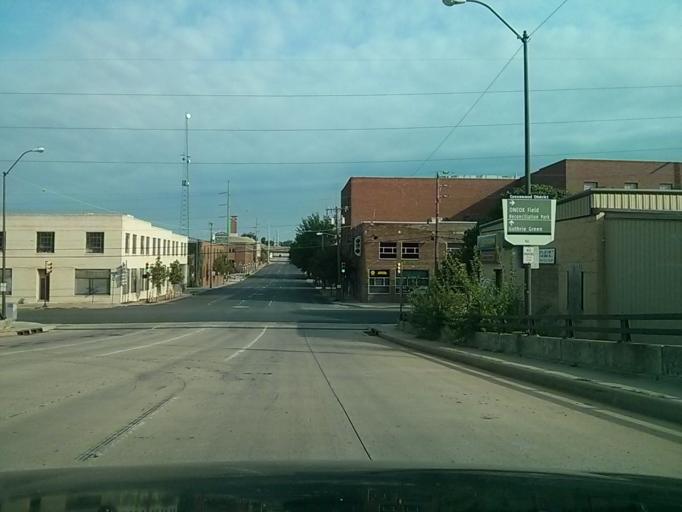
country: US
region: Oklahoma
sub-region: Tulsa County
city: Tulsa
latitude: 36.1581
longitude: -95.9893
